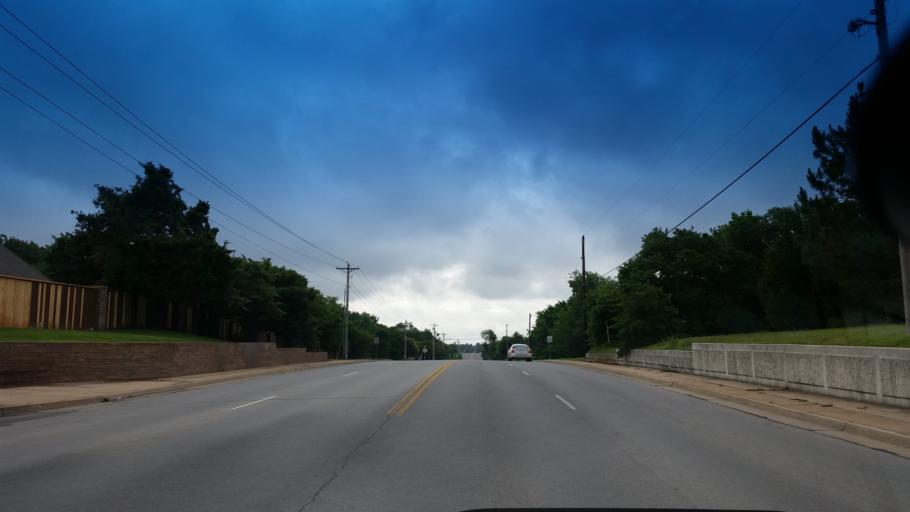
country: US
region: Oklahoma
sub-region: Oklahoma County
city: Edmond
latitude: 35.6383
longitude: -97.4363
